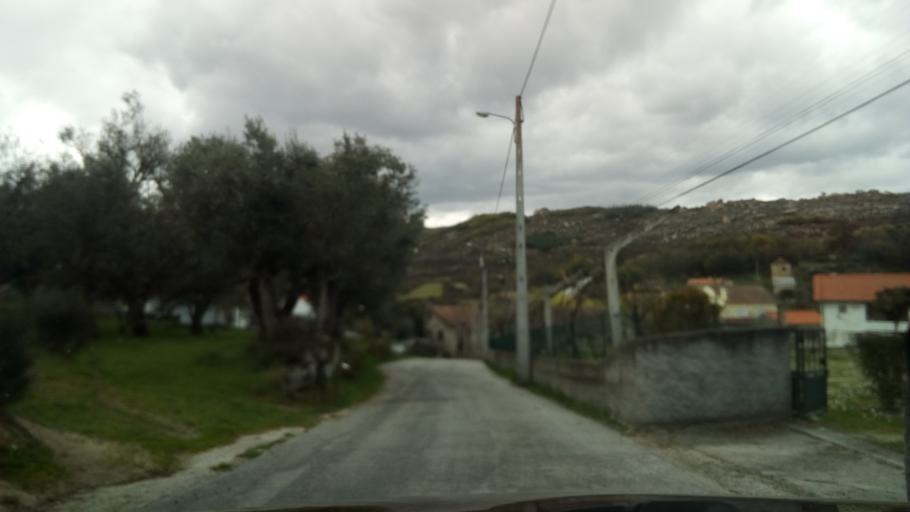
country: PT
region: Guarda
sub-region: Fornos de Algodres
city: Fornos de Algodres
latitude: 40.5852
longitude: -7.5650
